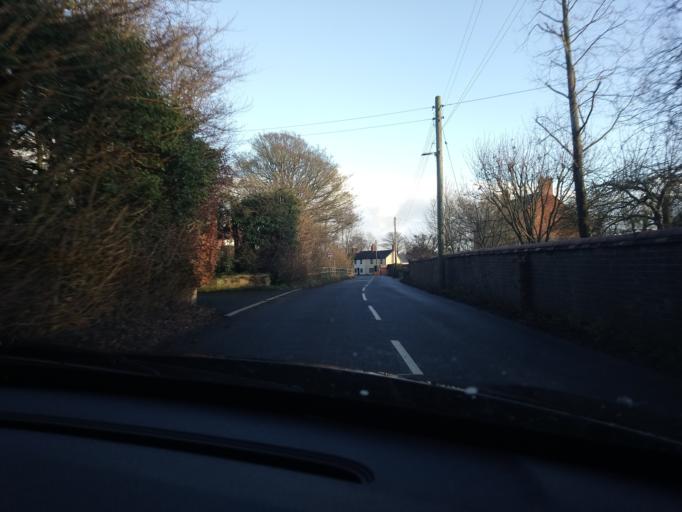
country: GB
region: England
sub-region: Shropshire
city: Wem
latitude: 52.8566
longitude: -2.7343
